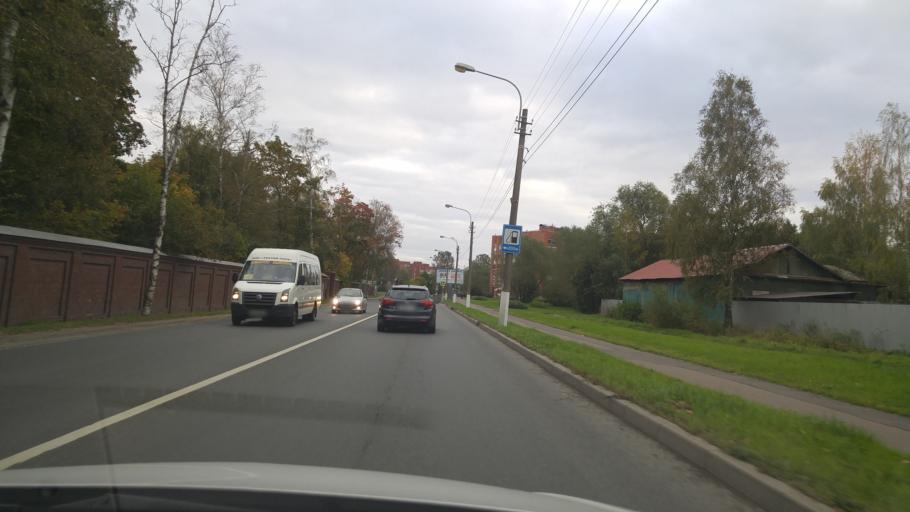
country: RU
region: St.-Petersburg
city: Kronshtadt
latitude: 60.0037
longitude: 29.7538
